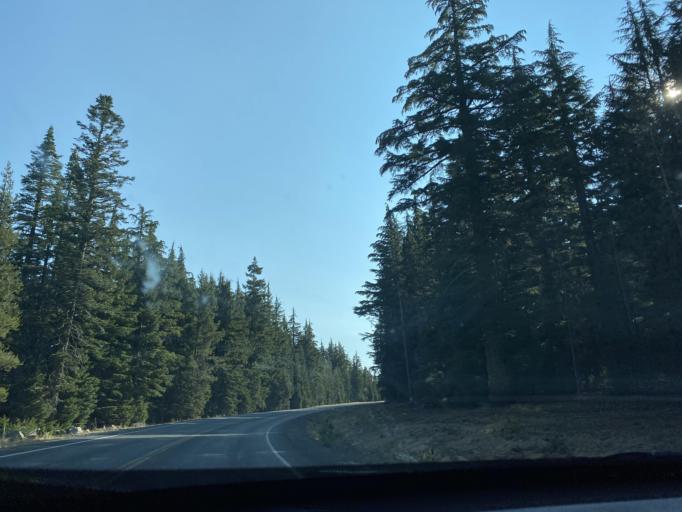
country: US
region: Oregon
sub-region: Deschutes County
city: Three Rivers
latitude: 43.7113
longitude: -121.2822
